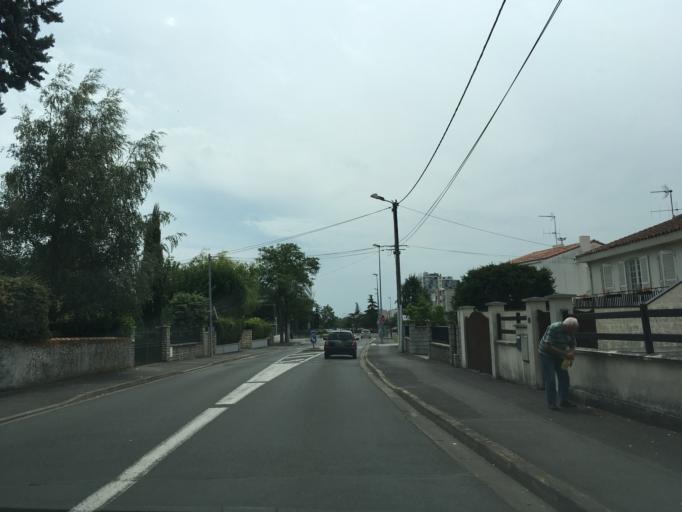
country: FR
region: Poitou-Charentes
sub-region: Departement des Deux-Sevres
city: Niort
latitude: 46.3185
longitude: -0.4799
